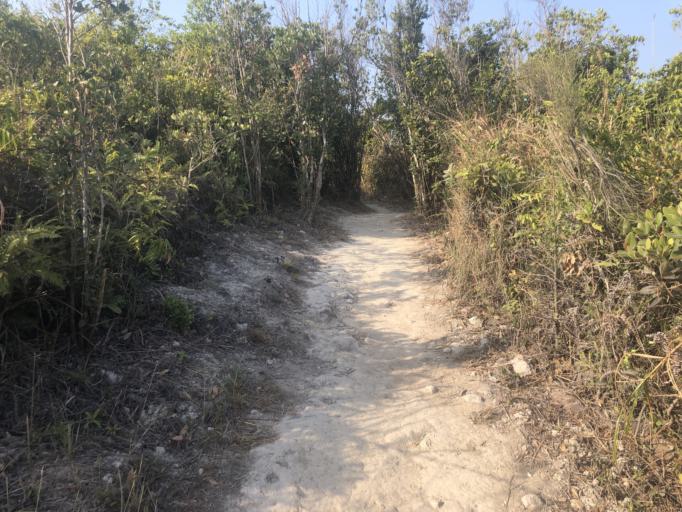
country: HK
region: Sai Kung
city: Sai Kung
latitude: 22.3609
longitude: 114.2945
